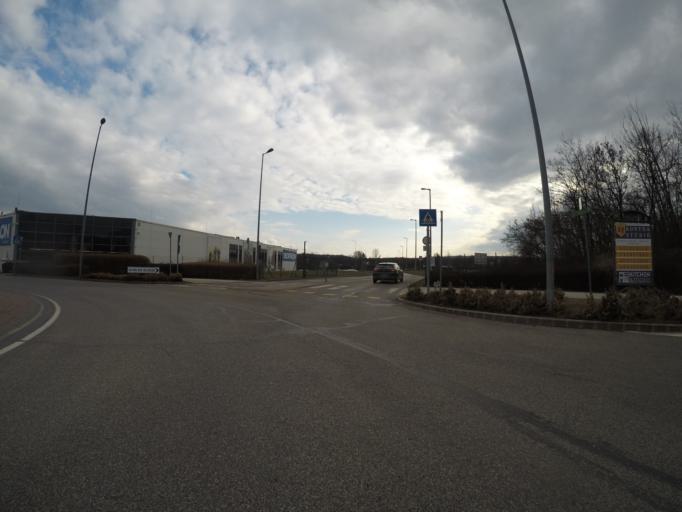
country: HU
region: Pest
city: Budaors
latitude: 47.4543
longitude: 18.9353
